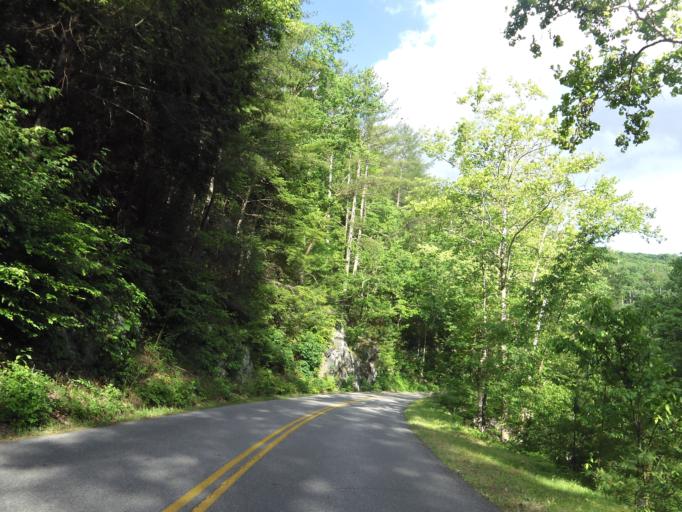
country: US
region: Tennessee
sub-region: Sevier County
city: Gatlinburg
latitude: 35.6711
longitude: -83.6641
